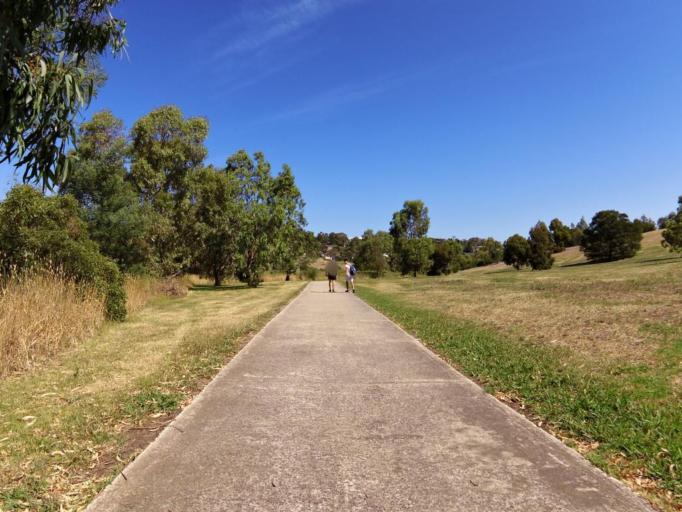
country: AU
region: Victoria
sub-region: Hume
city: Broadmeadows
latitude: -37.6725
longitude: 144.9119
